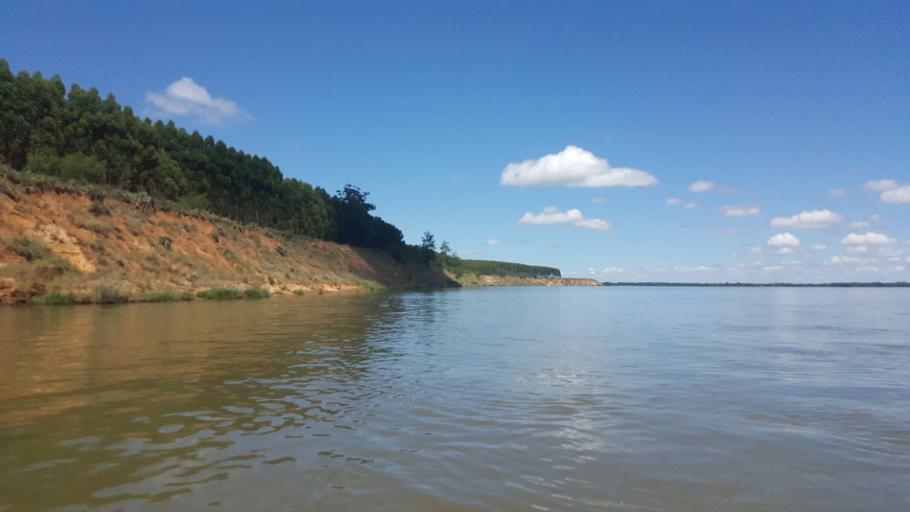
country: AR
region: Corrientes
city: Ituzaingo
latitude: -27.5951
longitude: -56.7830
